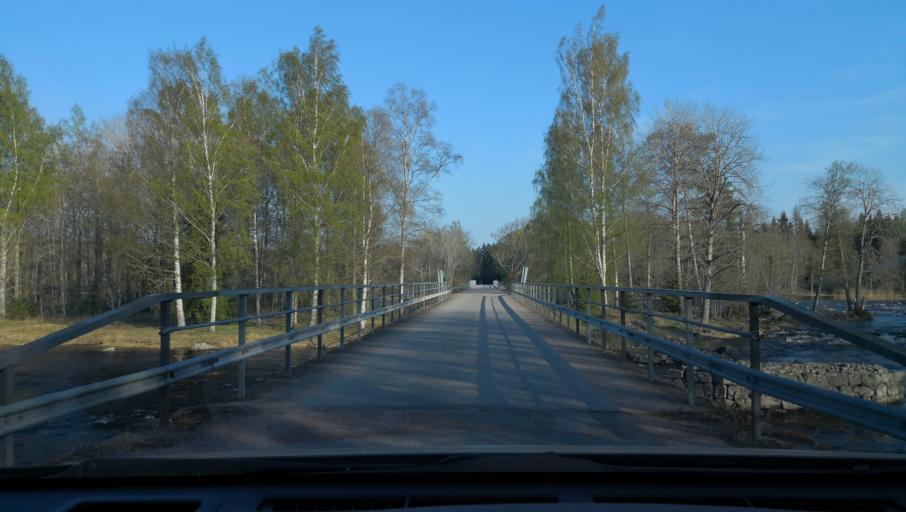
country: SE
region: Uppsala
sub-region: Heby Kommun
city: Tarnsjo
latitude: 60.2683
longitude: 16.9122
